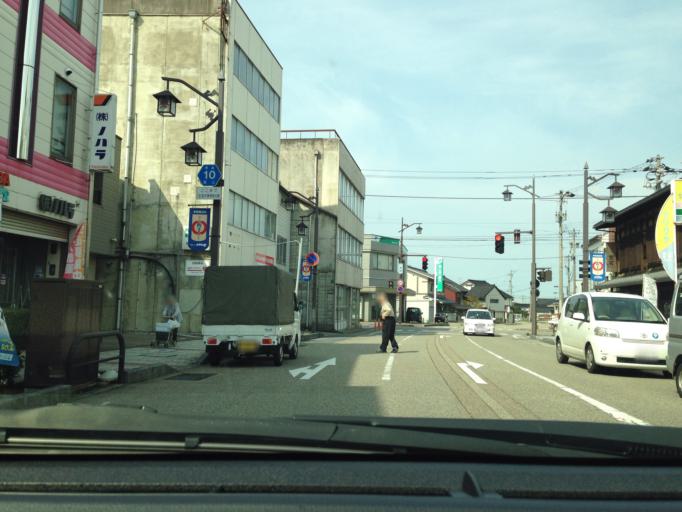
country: JP
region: Toyama
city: Fukumitsu
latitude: 36.5594
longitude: 136.8725
